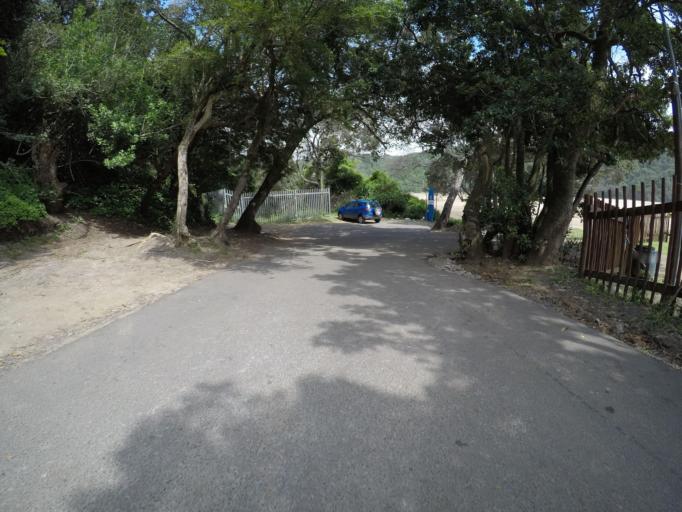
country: ZA
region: Eastern Cape
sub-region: Buffalo City Metropolitan Municipality
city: East London
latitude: -32.9332
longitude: 28.0285
